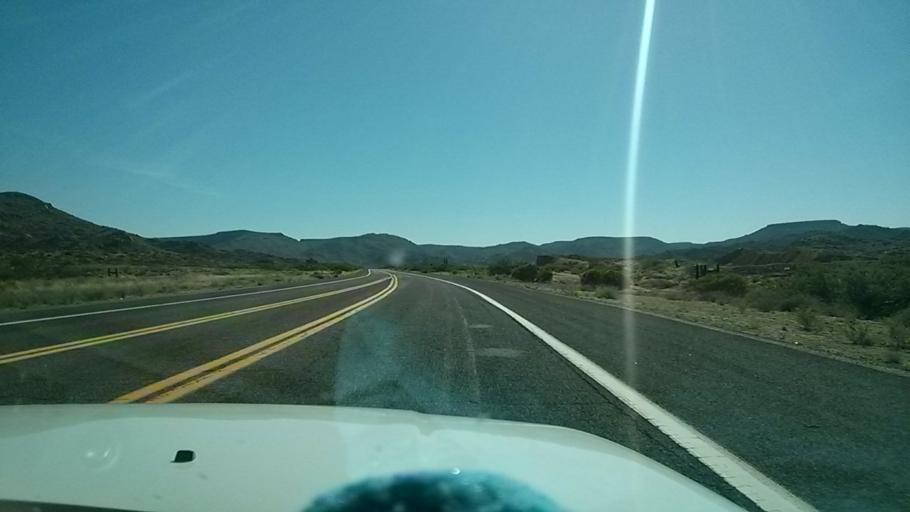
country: US
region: Arizona
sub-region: Mohave County
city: Peach Springs
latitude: 35.3619
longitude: -113.6885
